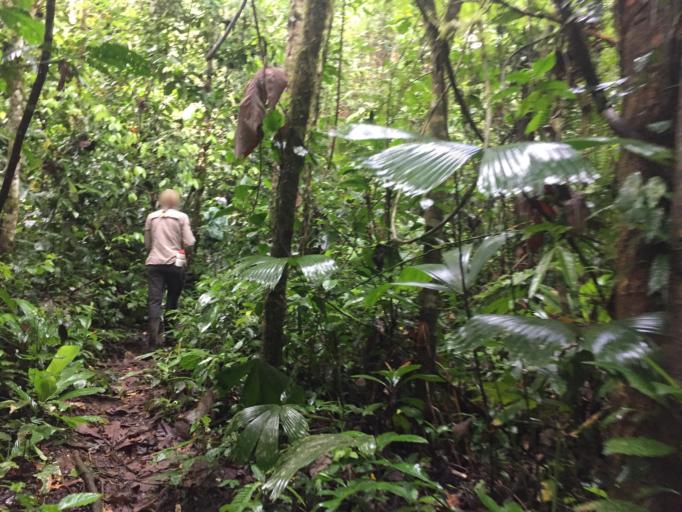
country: PE
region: Cusco
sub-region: Provincia de Paucartambo
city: Pillcopata
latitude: -12.8160
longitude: -71.4002
